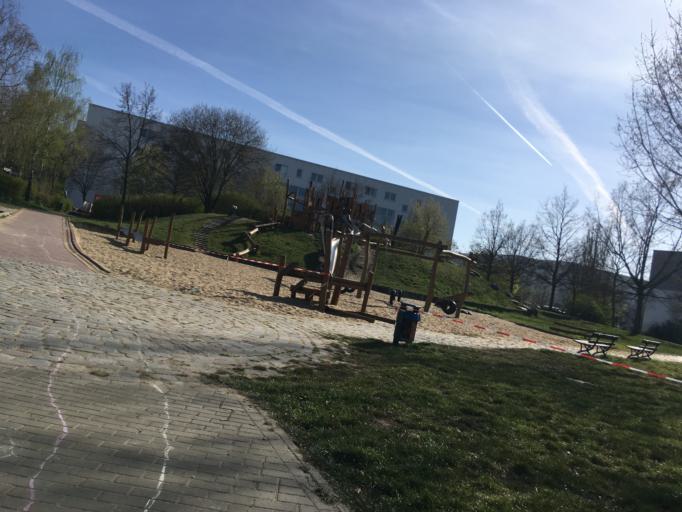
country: DE
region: Berlin
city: Wartenberg
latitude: 52.5781
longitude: 13.5067
